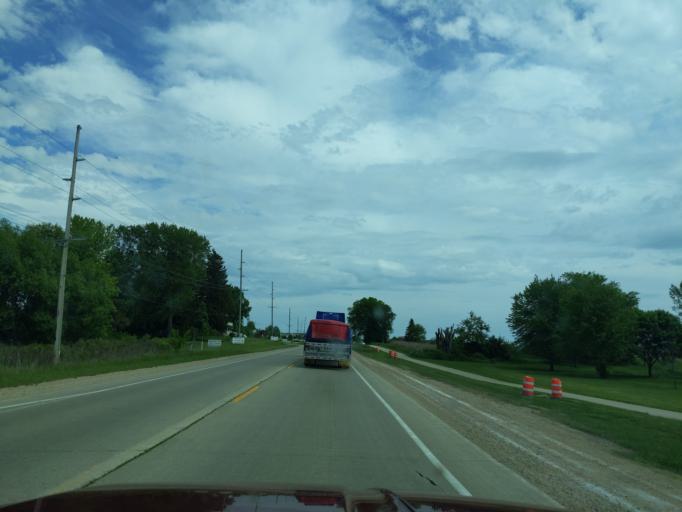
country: US
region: Wisconsin
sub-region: Dane County
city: Sun Prairie
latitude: 43.1889
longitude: -89.2753
